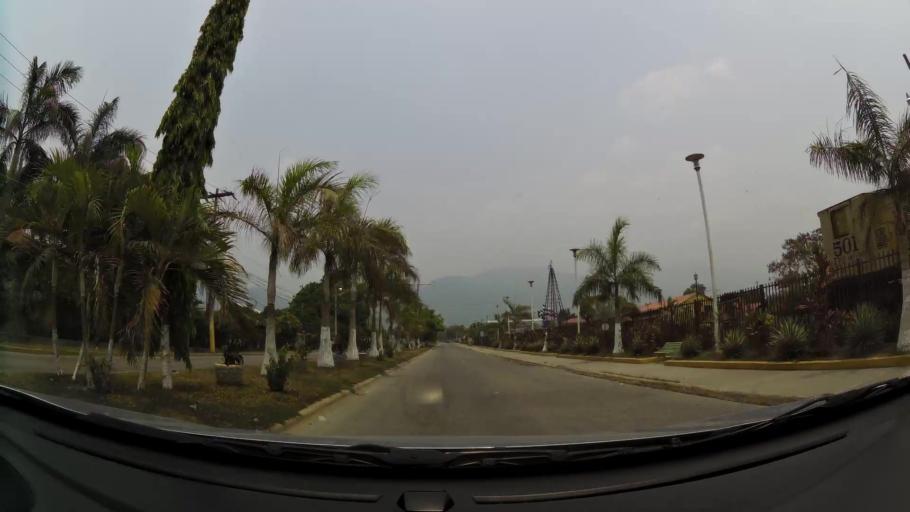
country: HN
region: Yoro
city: El Progreso
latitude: 15.3950
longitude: -87.8108
